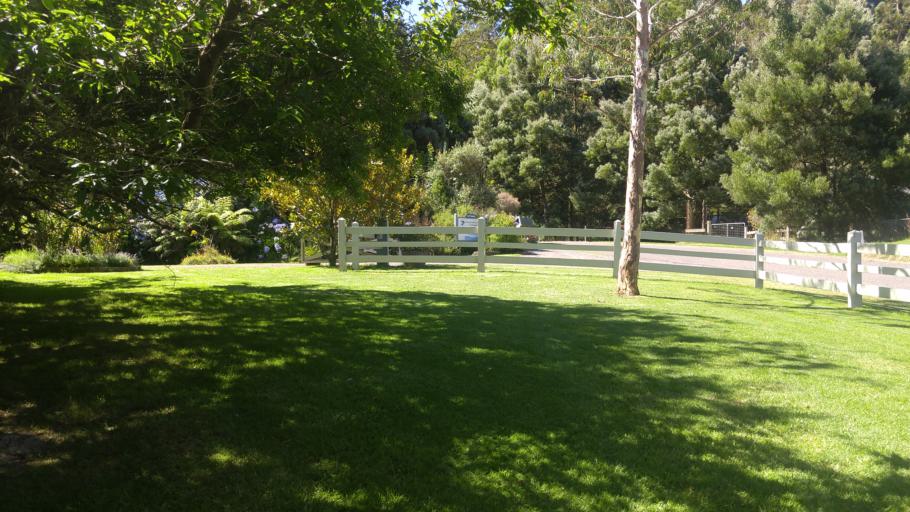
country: AU
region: Victoria
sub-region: Colac-Otway
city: Apollo Bay
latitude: -38.7419
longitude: 143.6247
